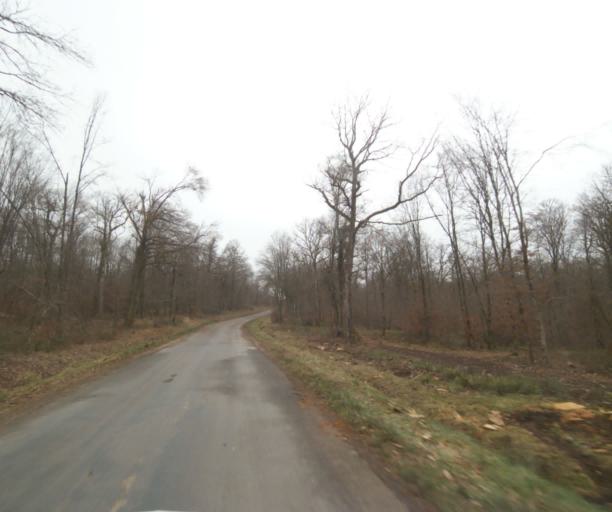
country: FR
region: Champagne-Ardenne
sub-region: Departement de la Haute-Marne
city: Wassy
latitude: 48.5350
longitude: 4.9813
